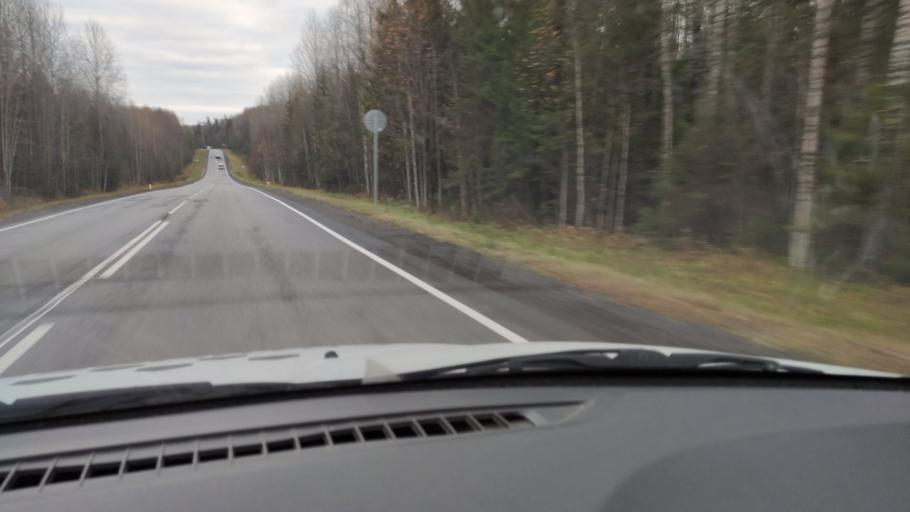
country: RU
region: Kirov
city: Chernaya Kholunitsa
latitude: 58.8599
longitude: 51.6195
